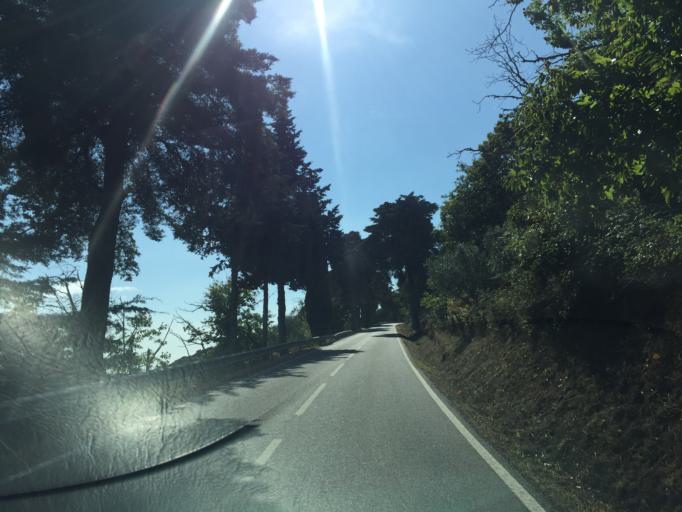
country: PT
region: Portalegre
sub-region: Marvao
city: Marvao
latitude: 39.3984
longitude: -7.3772
